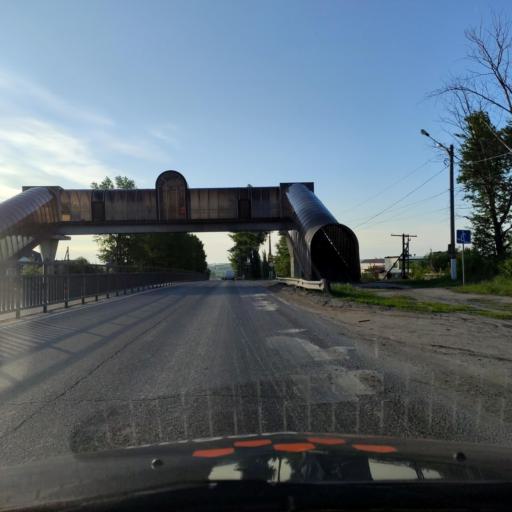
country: RU
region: Lipetsk
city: Yelets
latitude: 52.5946
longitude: 38.4830
